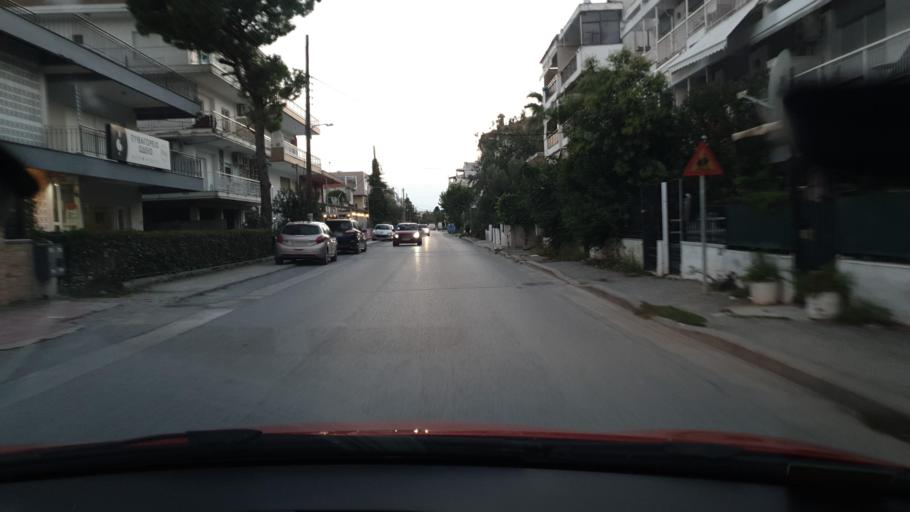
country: GR
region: Central Macedonia
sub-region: Nomos Thessalonikis
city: Peraia
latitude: 40.5075
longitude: 22.9226
